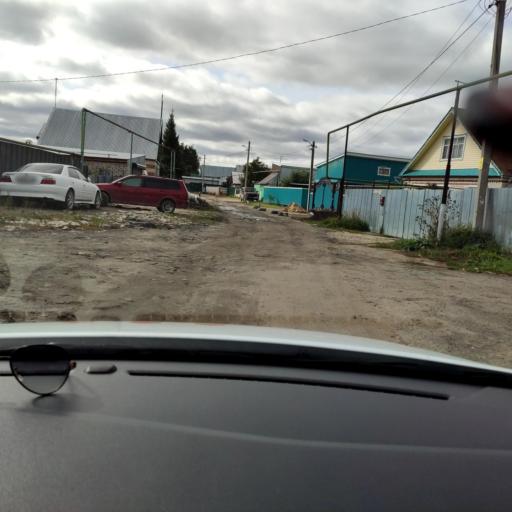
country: RU
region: Tatarstan
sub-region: Gorod Kazan'
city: Kazan
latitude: 55.7198
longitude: 49.1036
